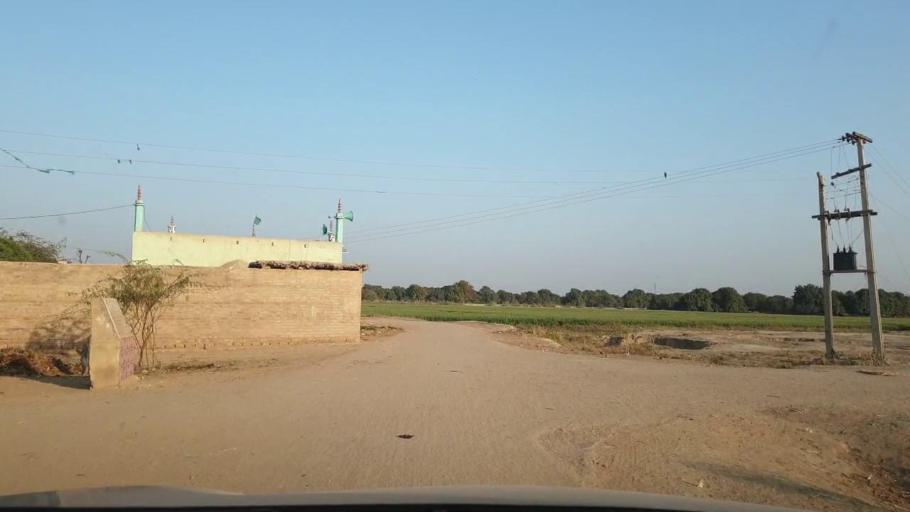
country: PK
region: Sindh
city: Tando Allahyar
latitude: 25.5657
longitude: 68.7915
